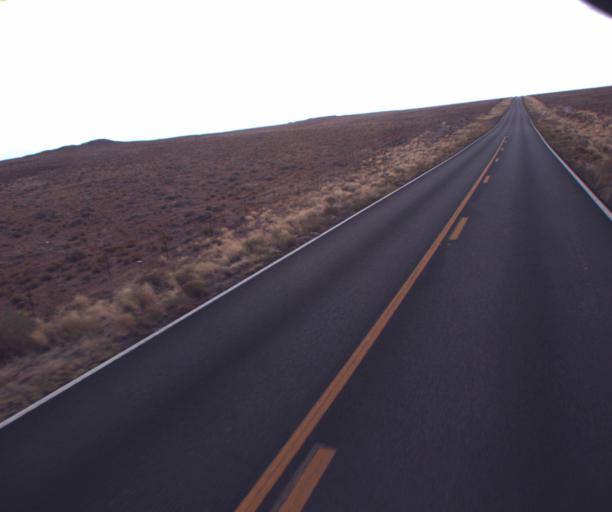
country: US
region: Arizona
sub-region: Apache County
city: Many Farms
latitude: 36.5805
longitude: -109.5547
